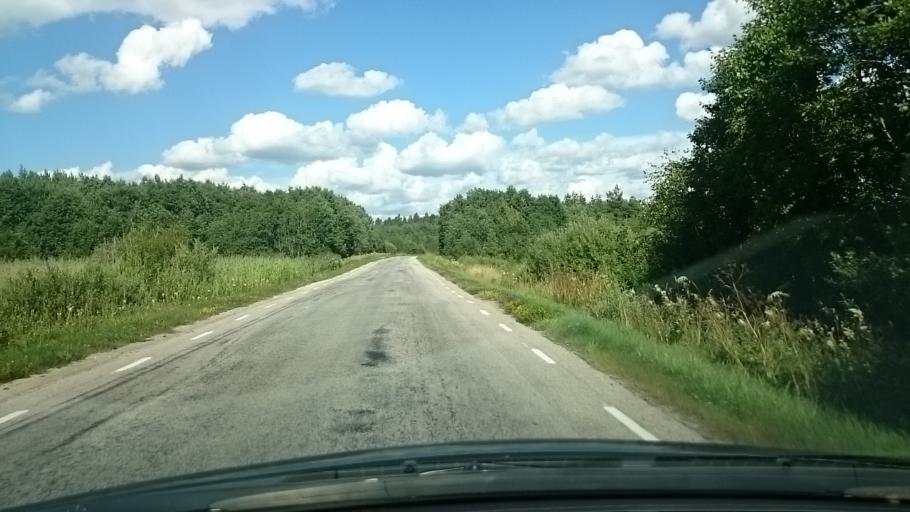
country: EE
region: Laeaene
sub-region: Haapsalu linn
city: Haapsalu
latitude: 59.0560
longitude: 23.5395
